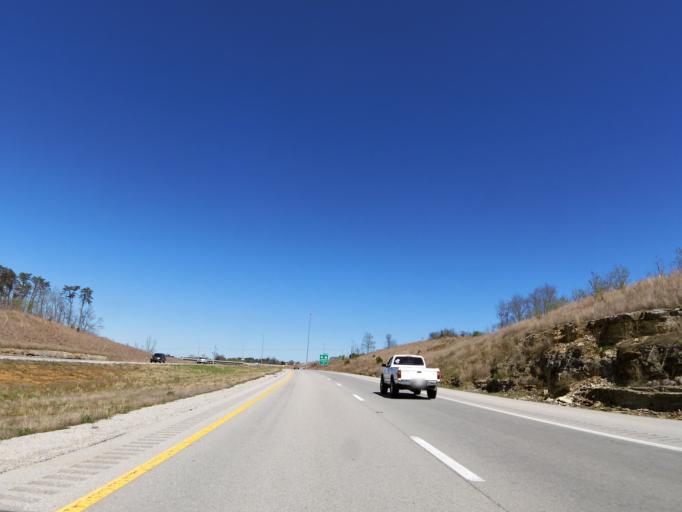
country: US
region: Kentucky
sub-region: Pulaski County
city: Somerset
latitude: 37.1007
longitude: -84.6690
